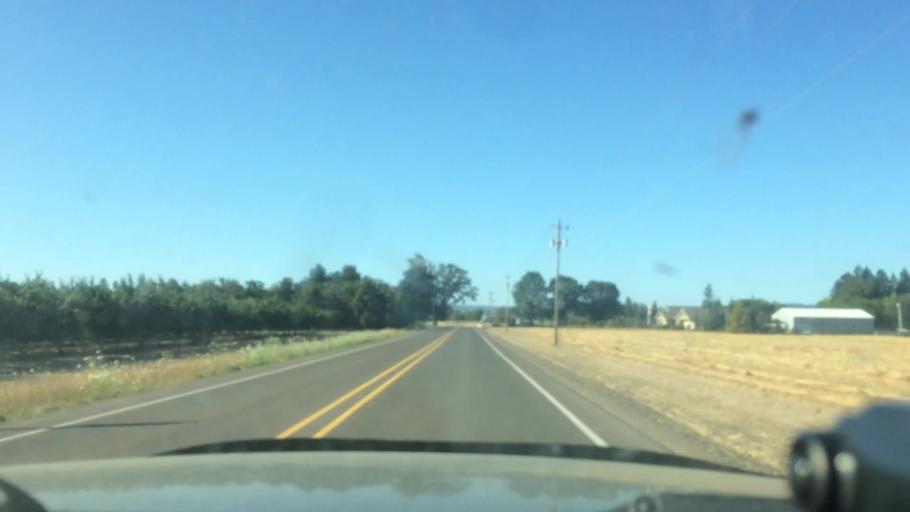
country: US
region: Oregon
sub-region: Yamhill County
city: Dundee
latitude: 45.1995
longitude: -122.9835
